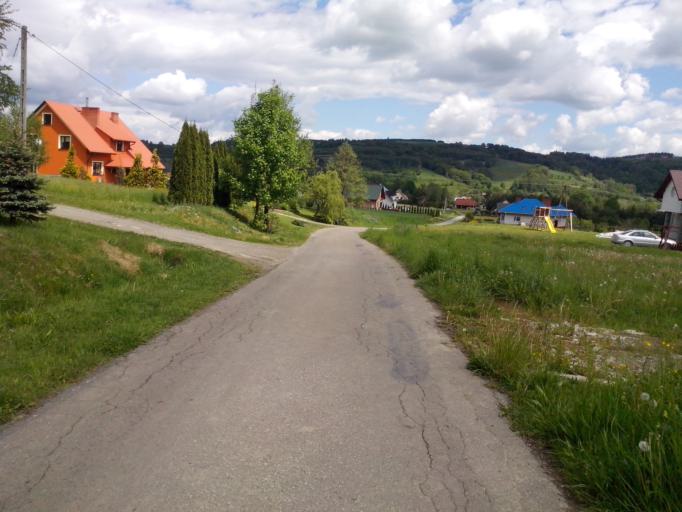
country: PL
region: Subcarpathian Voivodeship
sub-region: Powiat strzyzowski
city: Strzyzow
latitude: 49.8402
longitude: 21.8109
